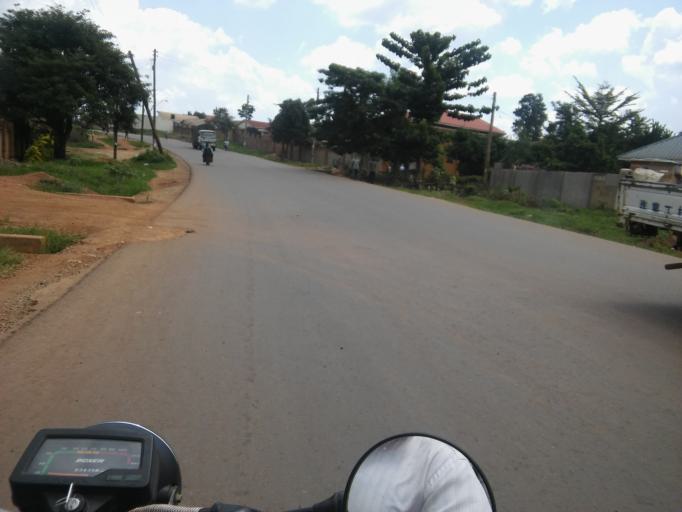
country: UG
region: Eastern Region
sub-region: Mbale District
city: Mbale
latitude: 1.0747
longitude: 34.1699
